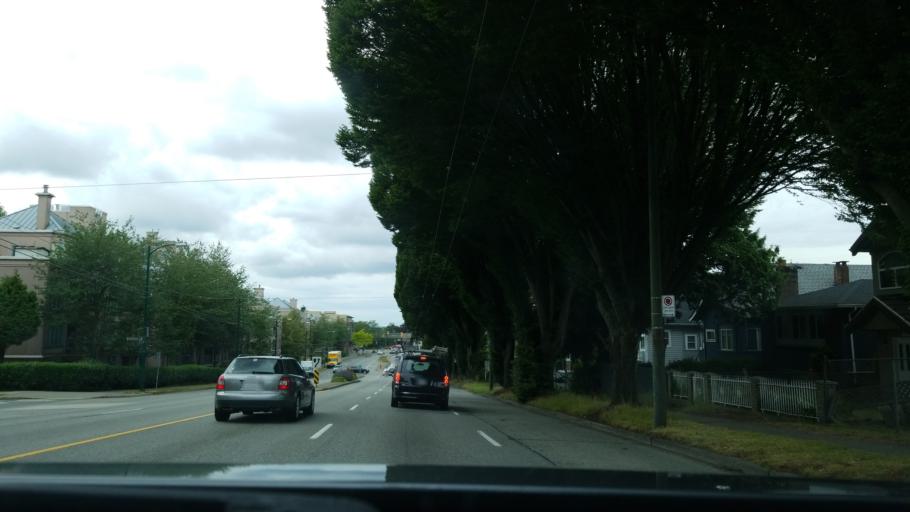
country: CA
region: British Columbia
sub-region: Fraser Valley Regional District
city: North Vancouver
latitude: 49.2620
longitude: -123.0526
